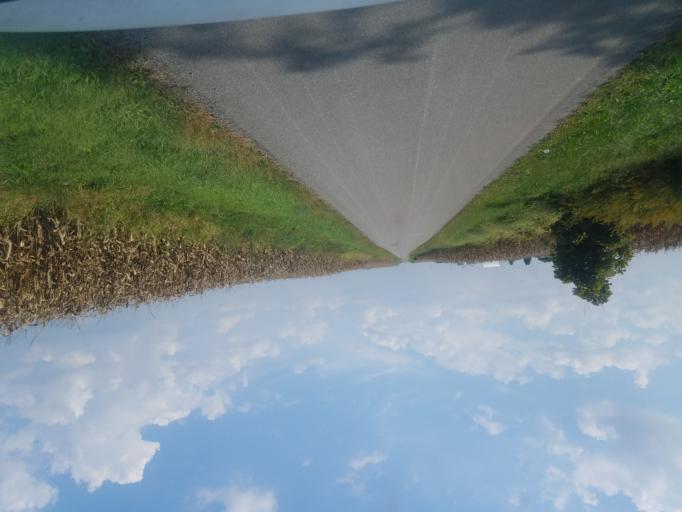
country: US
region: Ohio
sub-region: Hardin County
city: Ada
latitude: 40.6377
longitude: -83.8773
